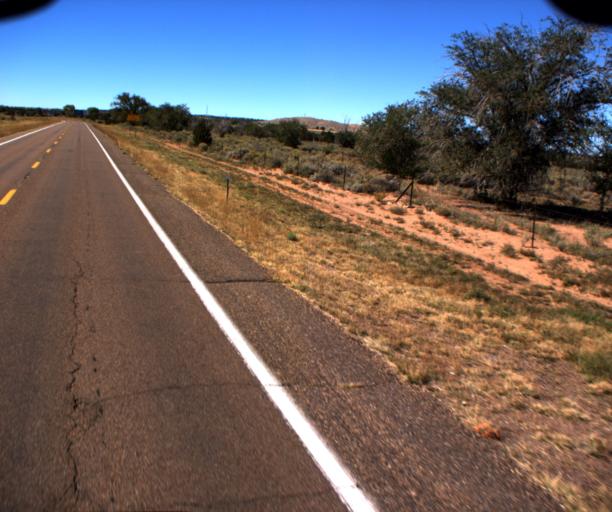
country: US
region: Arizona
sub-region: Apache County
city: Saint Johns
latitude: 34.4875
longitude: -109.3779
